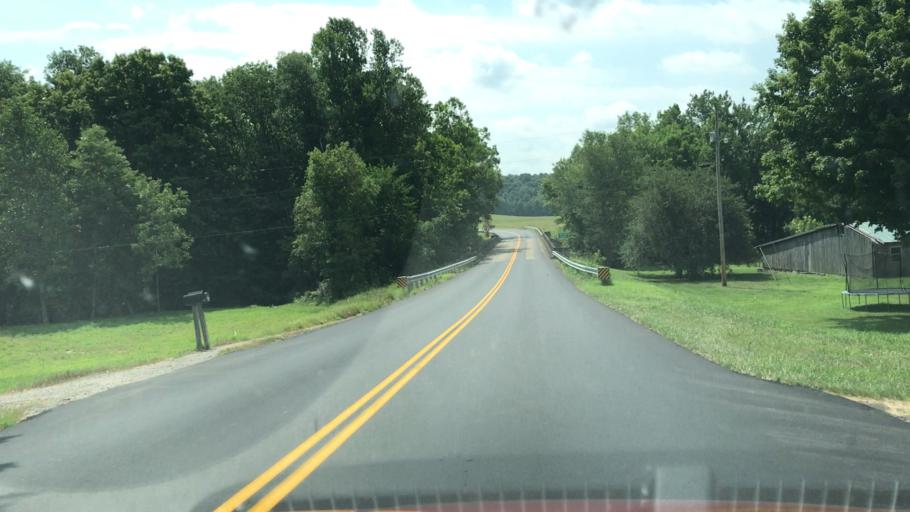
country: US
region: Kentucky
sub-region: Monroe County
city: Tompkinsville
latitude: 36.7389
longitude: -85.7556
